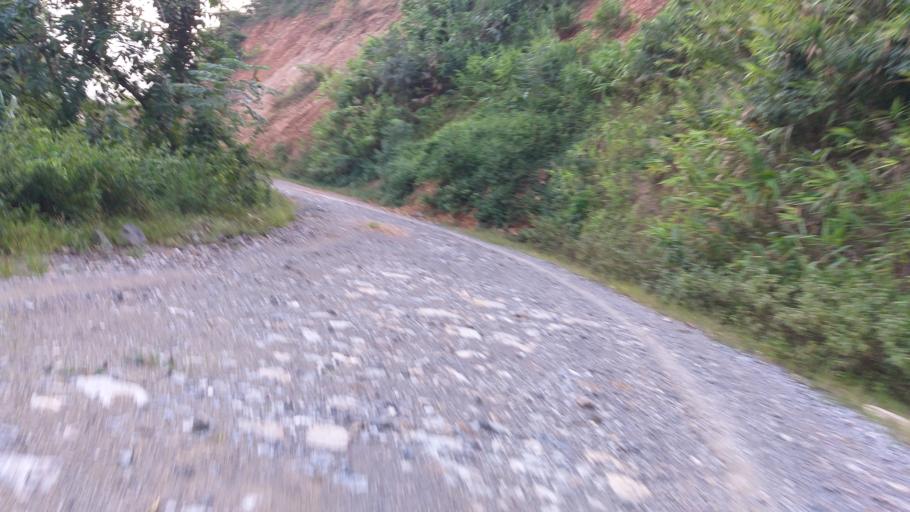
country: LA
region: Phongsali
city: Khoa
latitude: 21.1946
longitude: 102.5646
